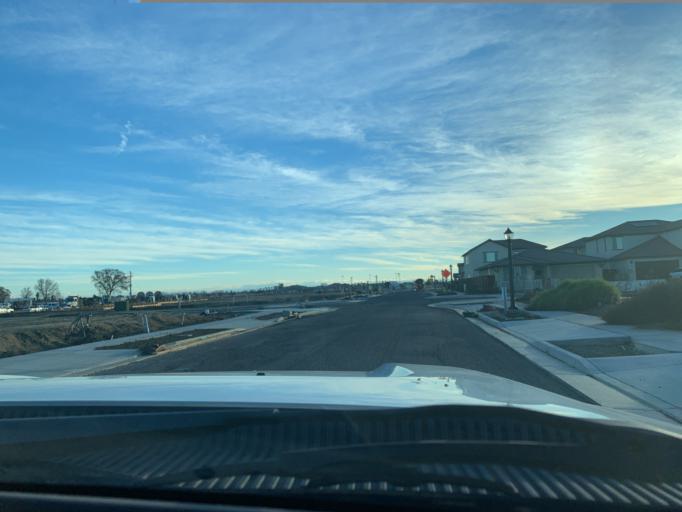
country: US
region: California
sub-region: Yolo County
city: Woodland
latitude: 38.6591
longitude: -121.7495
